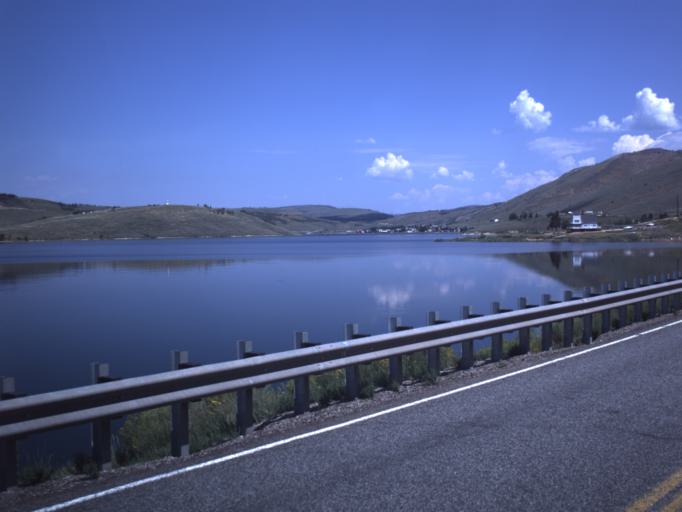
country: US
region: Utah
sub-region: Carbon County
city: Helper
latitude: 39.7792
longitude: -111.1353
